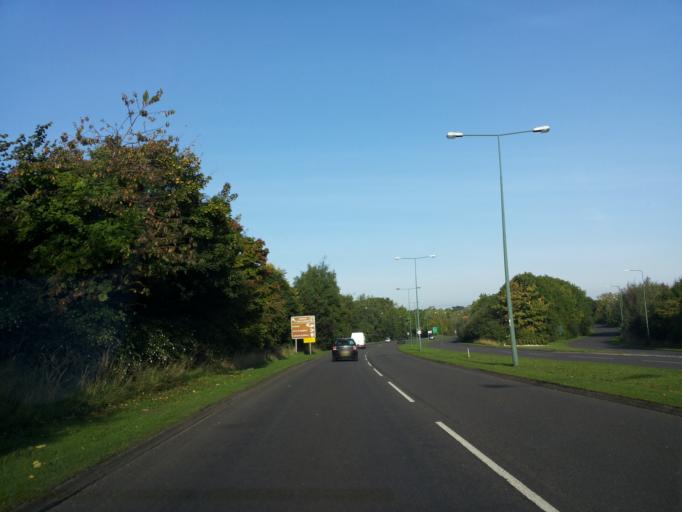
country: GB
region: England
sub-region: Solihull
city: Solihull
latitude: 52.4075
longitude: -1.7531
